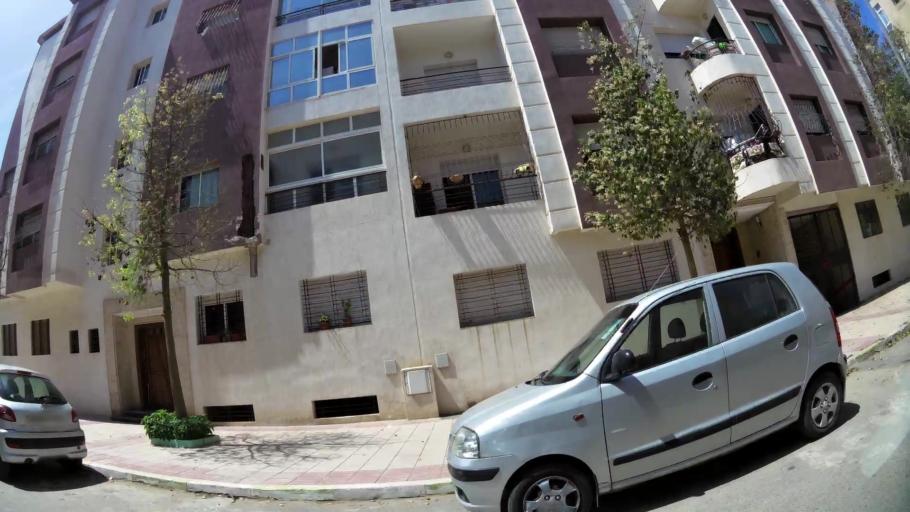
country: MA
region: Rabat-Sale-Zemmour-Zaer
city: Sale
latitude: 34.0775
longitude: -6.7894
